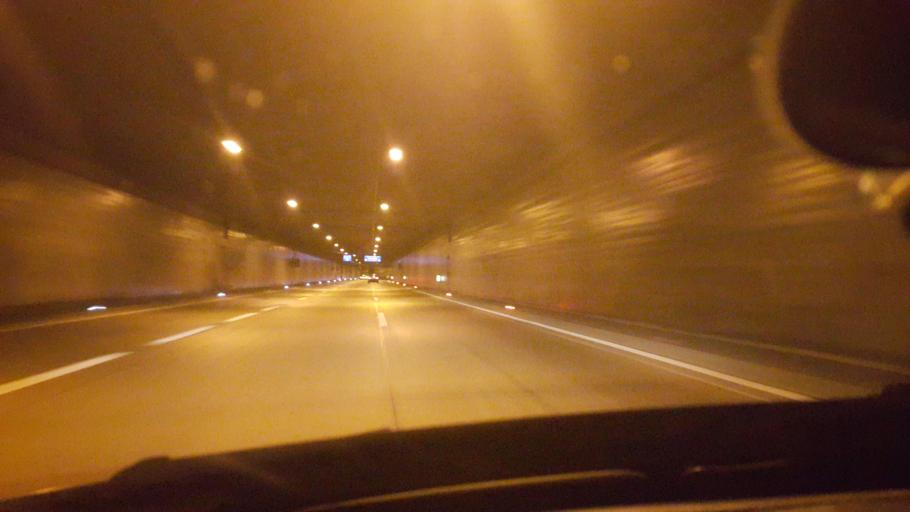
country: AT
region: Styria
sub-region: Graz Stadt
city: Wetzelsdorf
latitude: 47.0350
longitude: 15.4065
